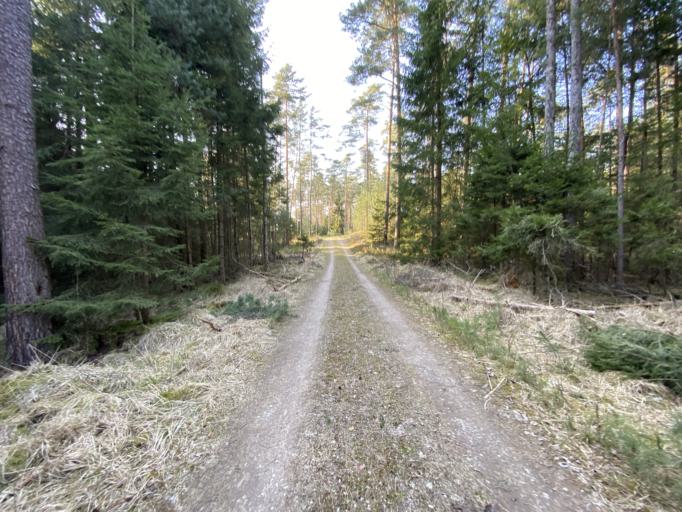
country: DE
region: Bavaria
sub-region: Regierungsbezirk Mittelfranken
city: Buckenhof
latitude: 49.5527
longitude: 11.0676
